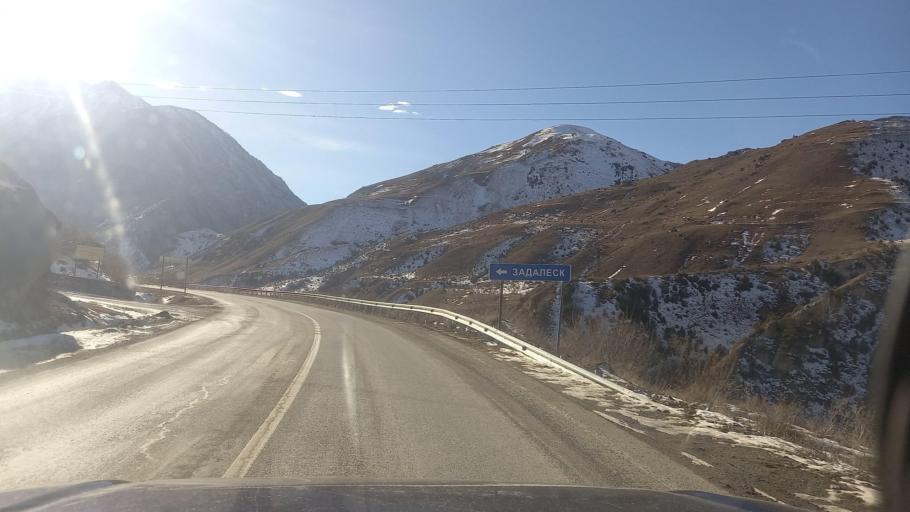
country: RU
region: North Ossetia
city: Chikola
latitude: 42.9966
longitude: 43.7846
